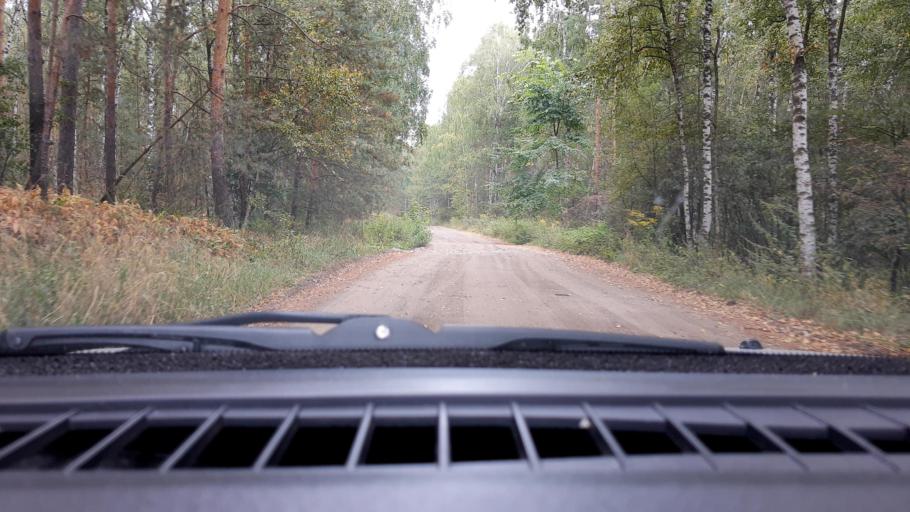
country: RU
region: Nizjnij Novgorod
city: Gorbatovka
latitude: 56.3130
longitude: 43.6907
